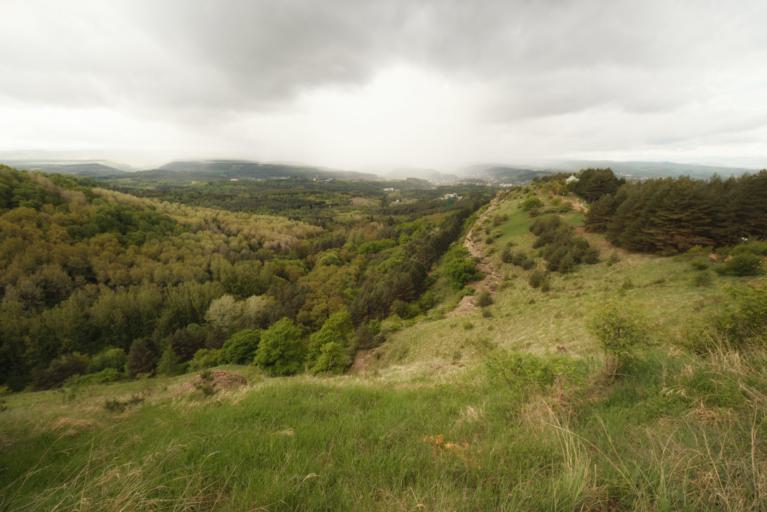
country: RU
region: Stavropol'skiy
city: Kislovodsk
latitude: 43.8999
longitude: 42.7544
